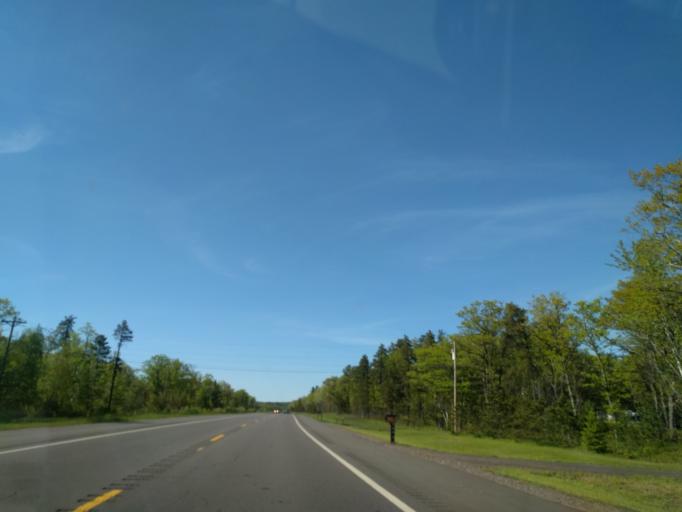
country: US
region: Michigan
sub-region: Marquette County
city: Harvey
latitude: 46.4550
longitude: -87.4256
